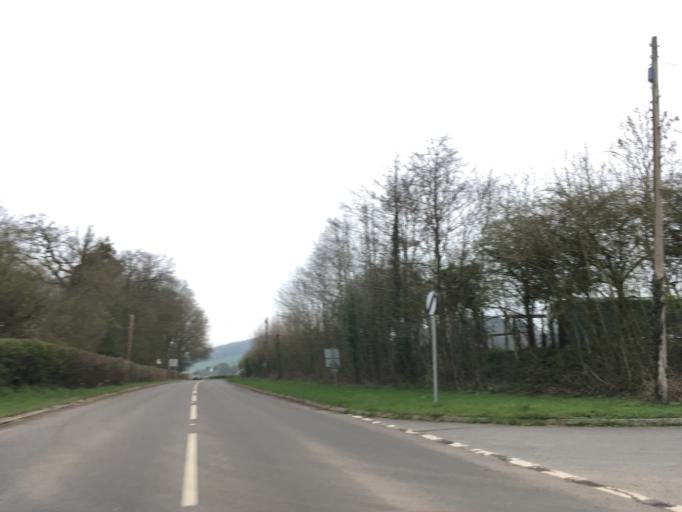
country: GB
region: Wales
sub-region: Monmouthshire
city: Usk
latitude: 51.7206
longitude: -2.9145
